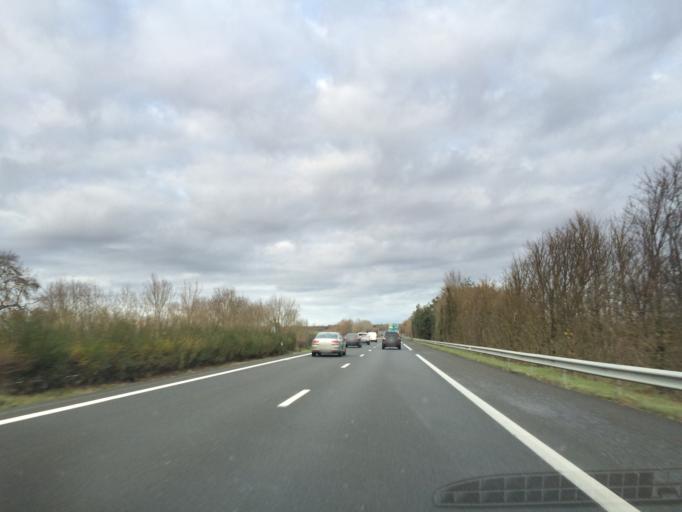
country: FR
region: Poitou-Charentes
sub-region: Departement de la Charente-Maritime
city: Saint-Jean-d'Angely
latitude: 46.0643
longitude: -0.5345
